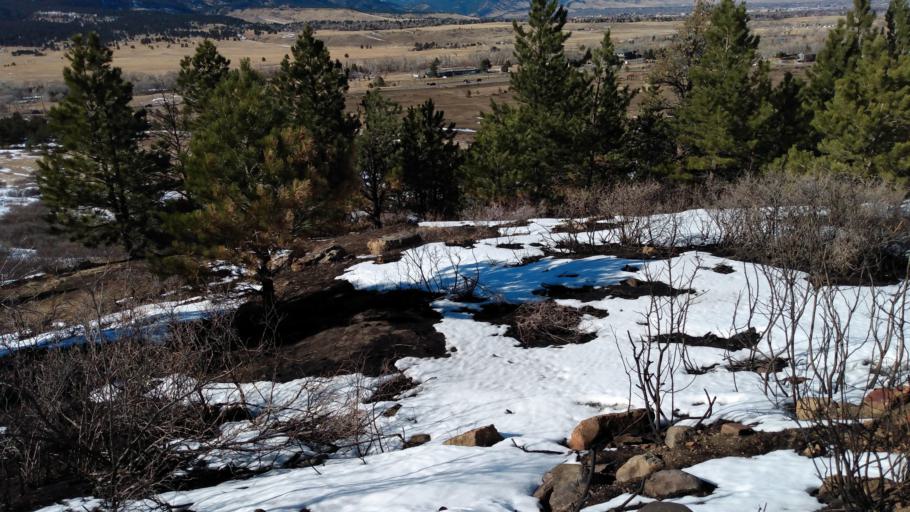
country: US
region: Colorado
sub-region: Boulder County
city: Superior
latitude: 39.9486
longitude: -105.2292
